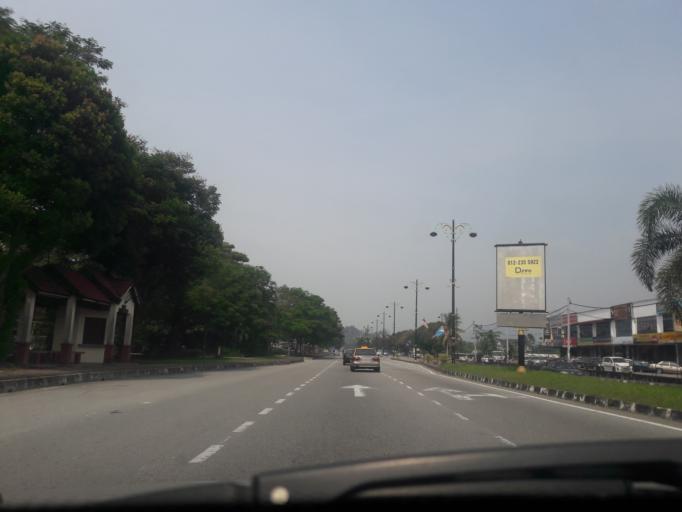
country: MY
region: Kedah
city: Kulim
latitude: 5.3856
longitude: 100.5586
